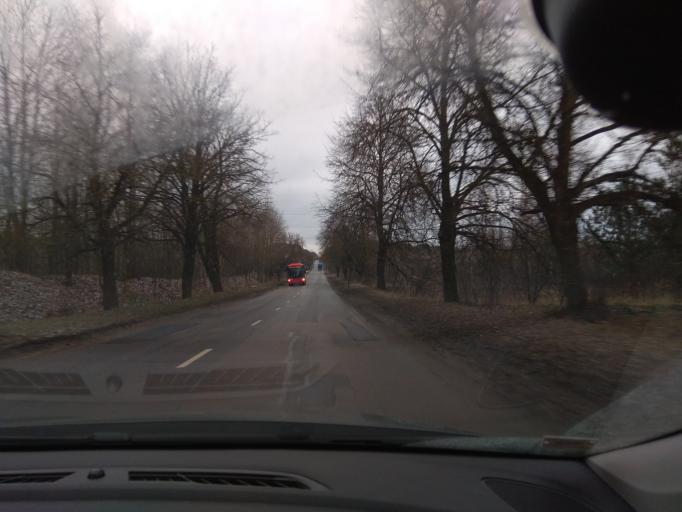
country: LT
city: Grigiskes
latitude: 54.6470
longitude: 25.1298
